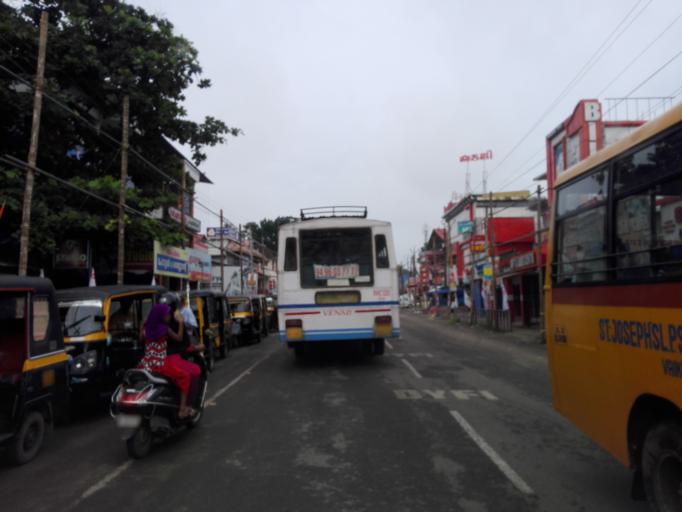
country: IN
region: Kerala
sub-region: Kottayam
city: Vaikam
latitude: 9.7497
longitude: 76.3925
